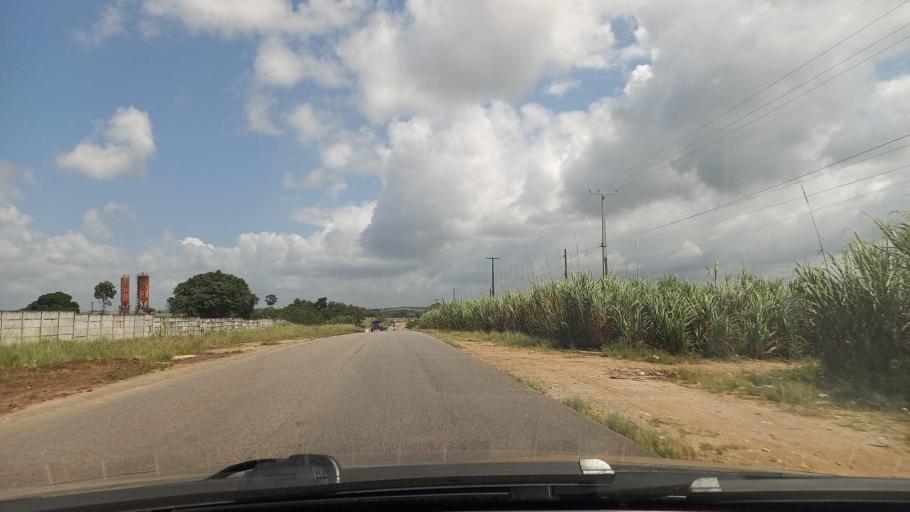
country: BR
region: Pernambuco
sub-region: Goiana
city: Goiana
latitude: -7.5579
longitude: -35.0311
